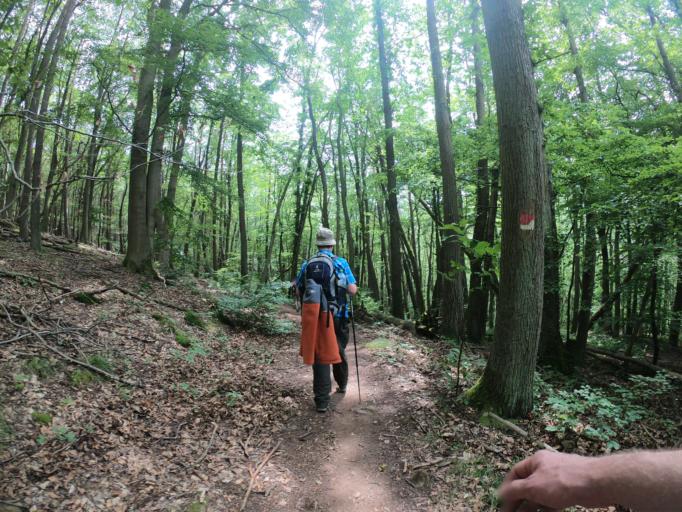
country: DE
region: Rheinland-Pfalz
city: Eschbach
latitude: 49.1617
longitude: 8.0084
